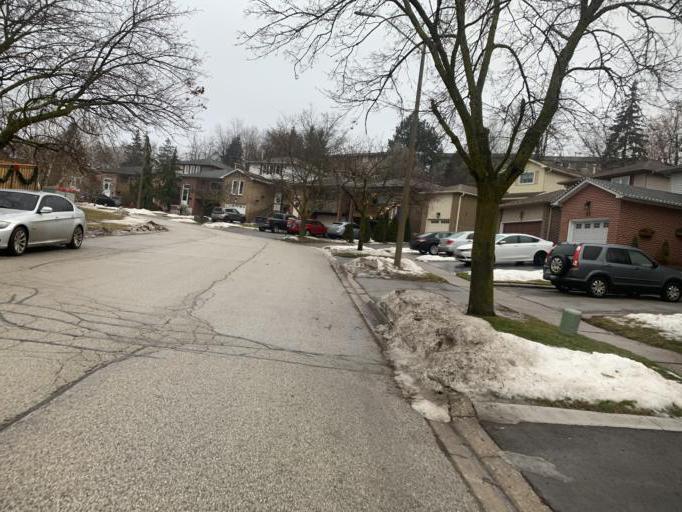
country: CA
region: Ontario
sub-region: Halton
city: Milton
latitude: 43.6591
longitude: -79.9169
